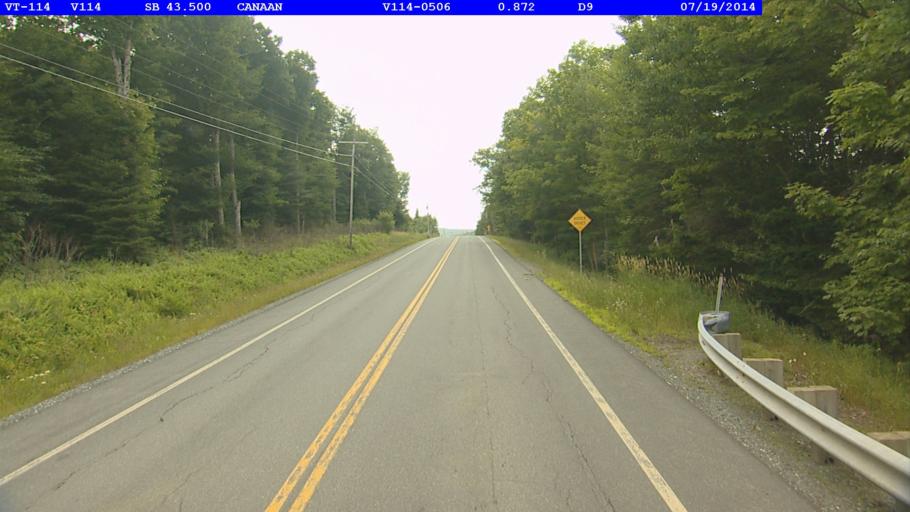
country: CA
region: Quebec
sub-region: Estrie
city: Coaticook
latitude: 45.0059
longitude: -71.6760
